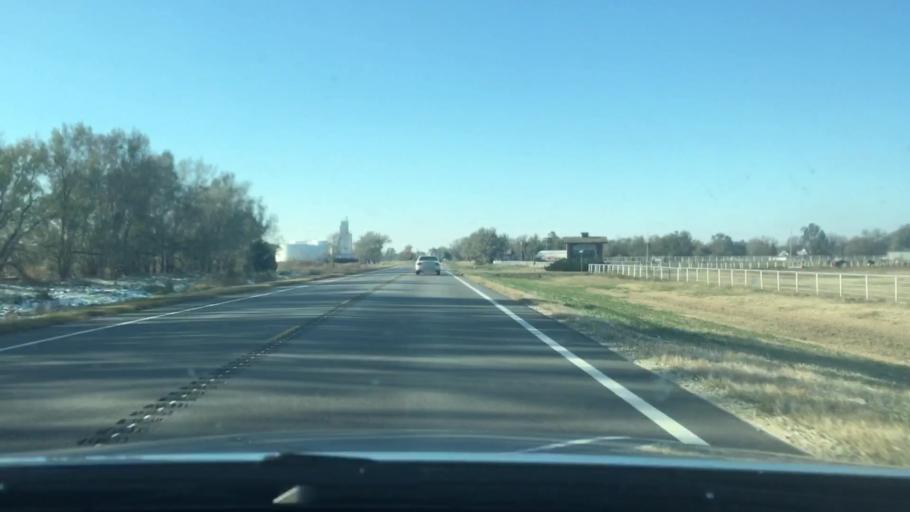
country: US
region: Kansas
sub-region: Reno County
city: Nickerson
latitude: 38.1399
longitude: -98.0728
